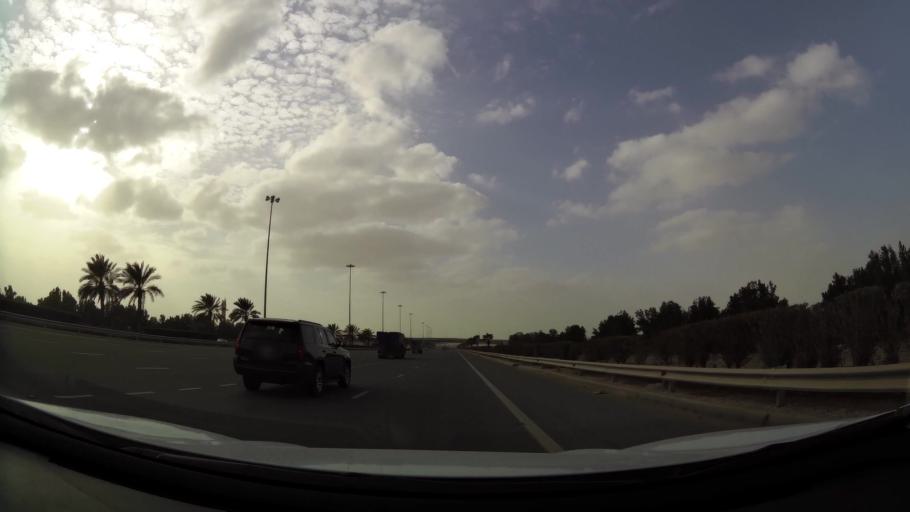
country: AE
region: Abu Dhabi
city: Abu Dhabi
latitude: 24.4909
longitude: 54.6241
